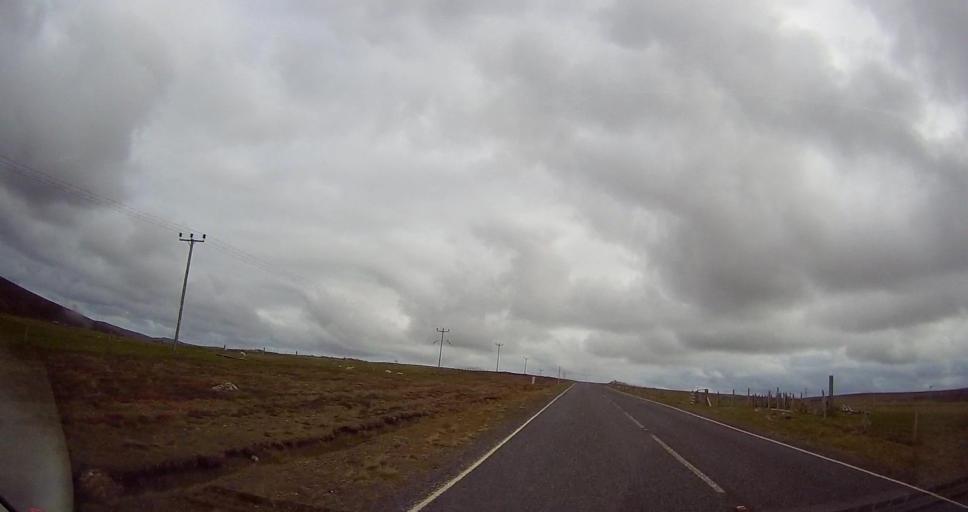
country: GB
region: Scotland
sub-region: Shetland Islands
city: Shetland
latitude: 60.7260
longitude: -0.9043
